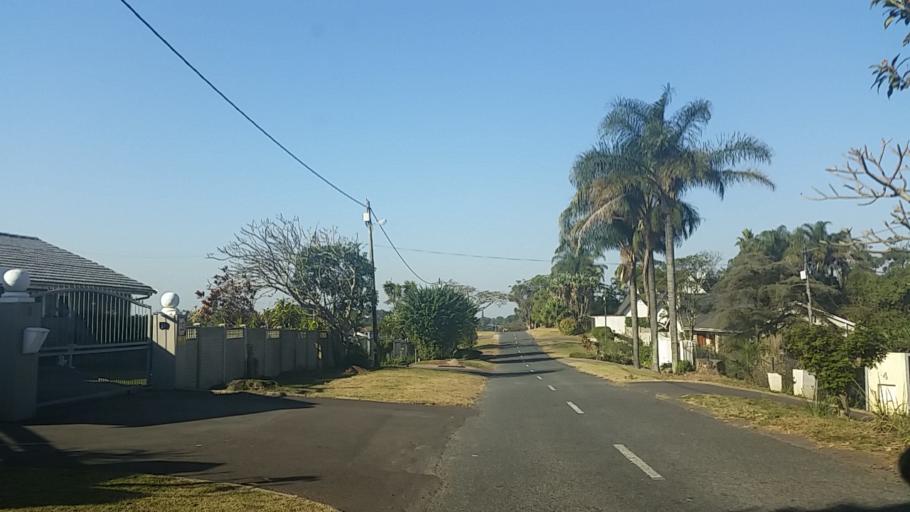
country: ZA
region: KwaZulu-Natal
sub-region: eThekwini Metropolitan Municipality
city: Berea
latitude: -29.8453
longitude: 30.9143
